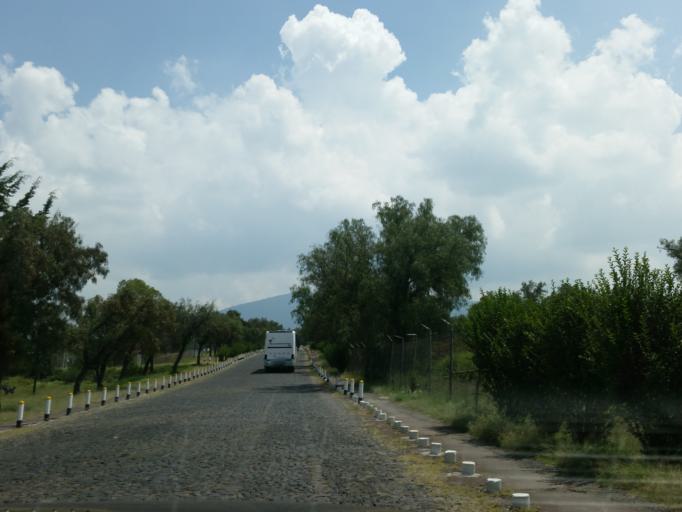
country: MX
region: Mexico
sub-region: Teotihuacan
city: Teotihuacan de Arista
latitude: 19.6902
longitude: -98.8503
